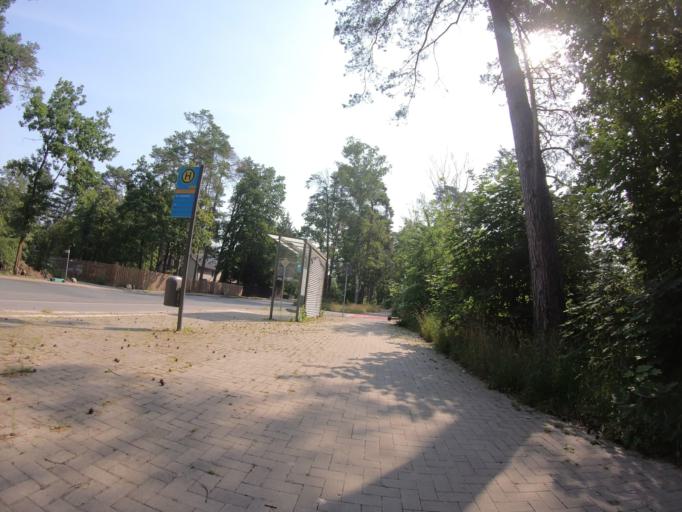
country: DE
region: Lower Saxony
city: Gifhorn
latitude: 52.4608
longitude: 10.5275
